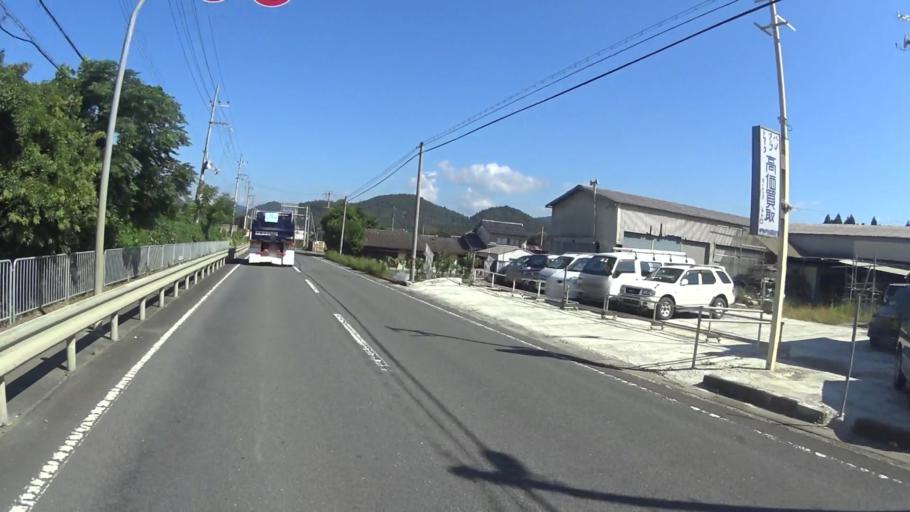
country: JP
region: Kyoto
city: Ayabe
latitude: 35.1680
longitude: 135.4241
